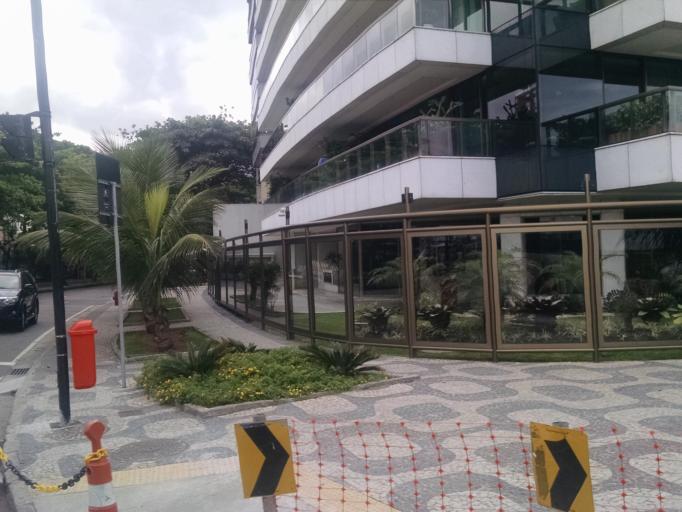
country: BR
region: Rio de Janeiro
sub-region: Rio De Janeiro
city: Rio de Janeiro
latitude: -22.9860
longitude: -43.2150
